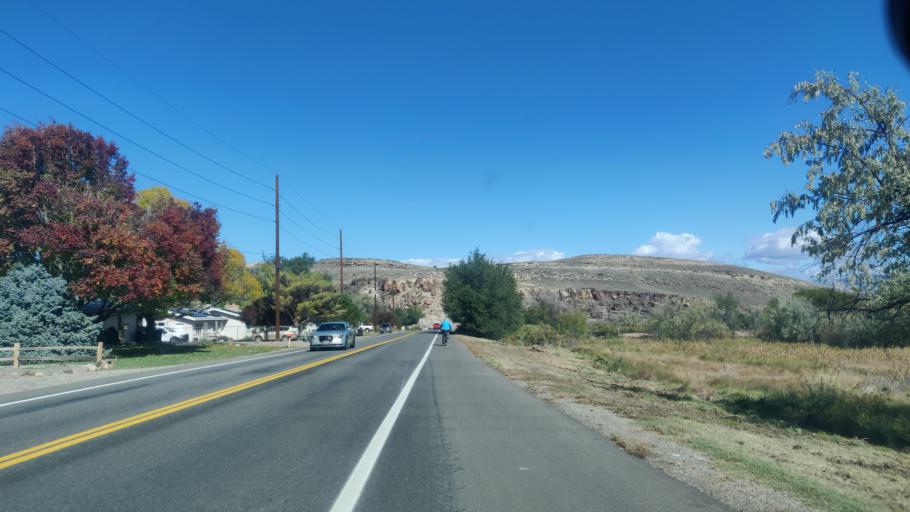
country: US
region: Colorado
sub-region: Mesa County
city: Redlands
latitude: 39.0694
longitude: -108.6449
